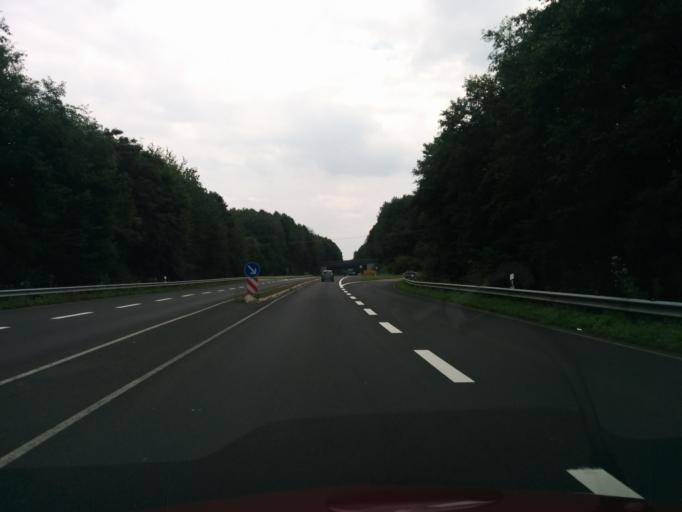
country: DE
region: Rheinland-Pfalz
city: Niederelbert
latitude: 50.4226
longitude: 7.8117
